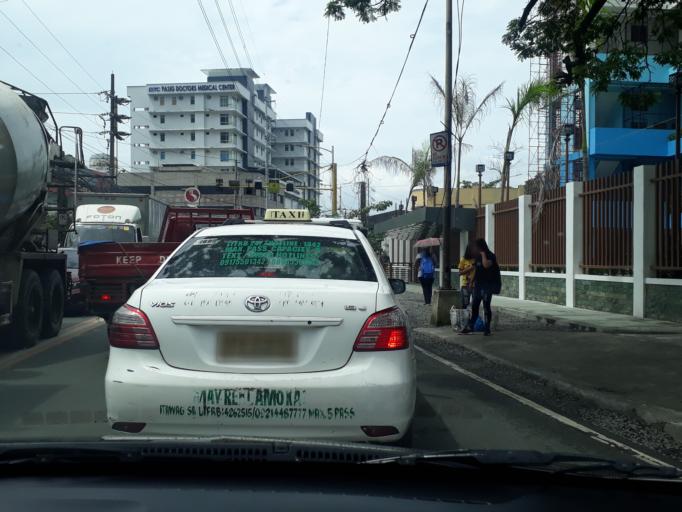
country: PH
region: Metro Manila
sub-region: Marikina
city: Calumpang
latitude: 14.6024
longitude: 121.0922
